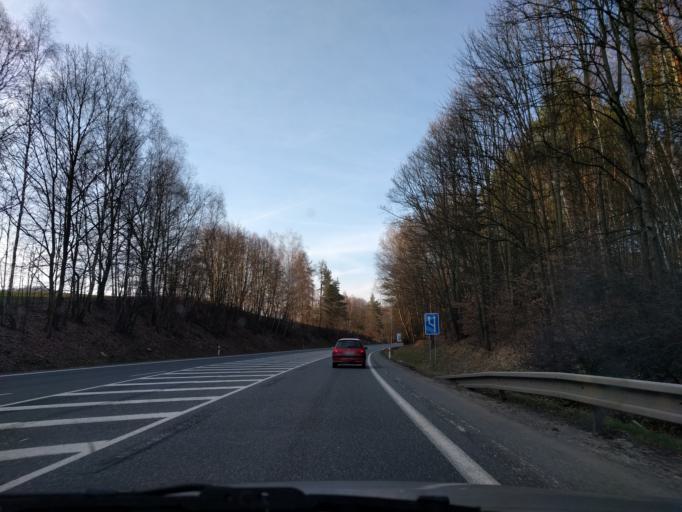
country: CZ
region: Central Bohemia
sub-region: Okres Benesov
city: Cercany
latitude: 49.8765
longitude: 14.7071
